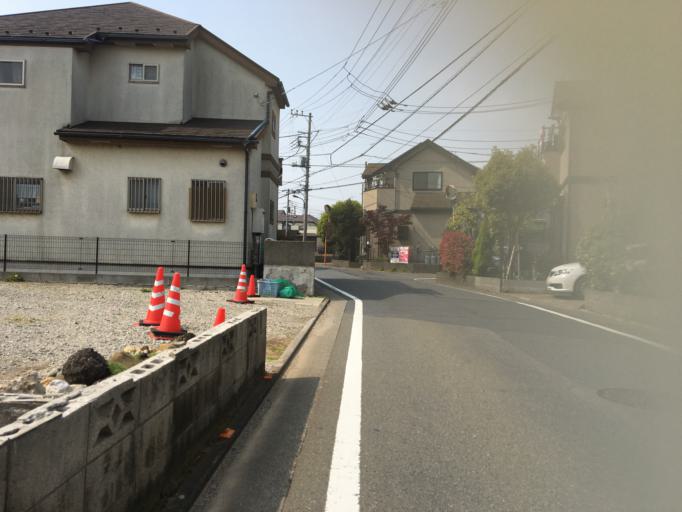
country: JP
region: Saitama
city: Shiki
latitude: 35.8038
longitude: 139.5446
